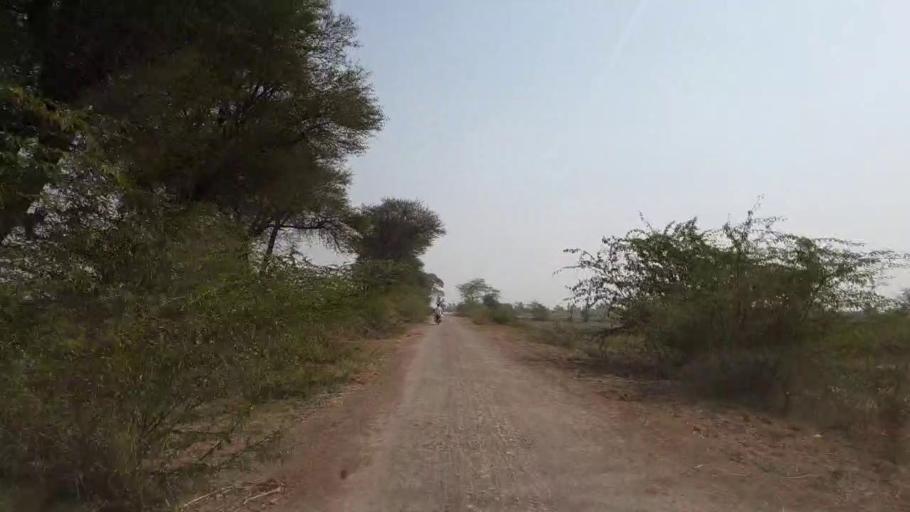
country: PK
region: Sindh
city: Mirpur Khas
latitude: 25.6050
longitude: 69.0226
